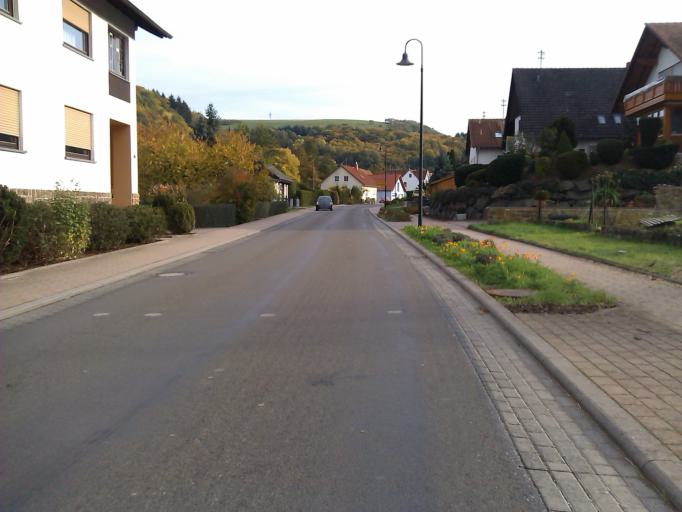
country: DE
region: Rheinland-Pfalz
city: Hefersweiler
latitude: 49.6070
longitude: 7.6862
